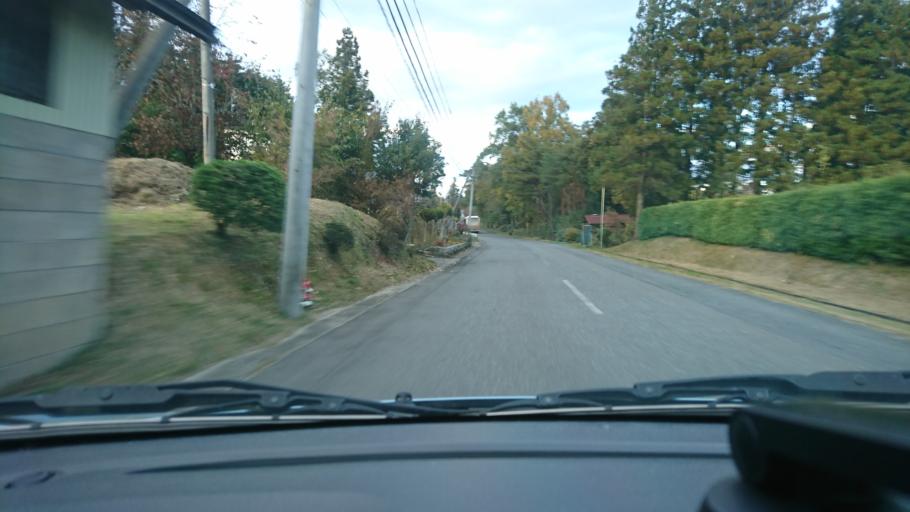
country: JP
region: Iwate
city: Ichinoseki
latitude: 38.7943
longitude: 141.1923
